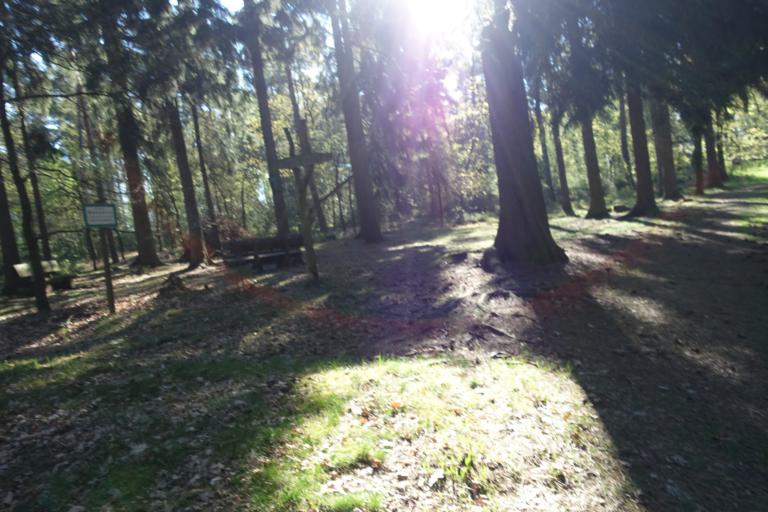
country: DE
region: Saxony
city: Freiberg
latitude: 50.8995
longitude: 13.3976
